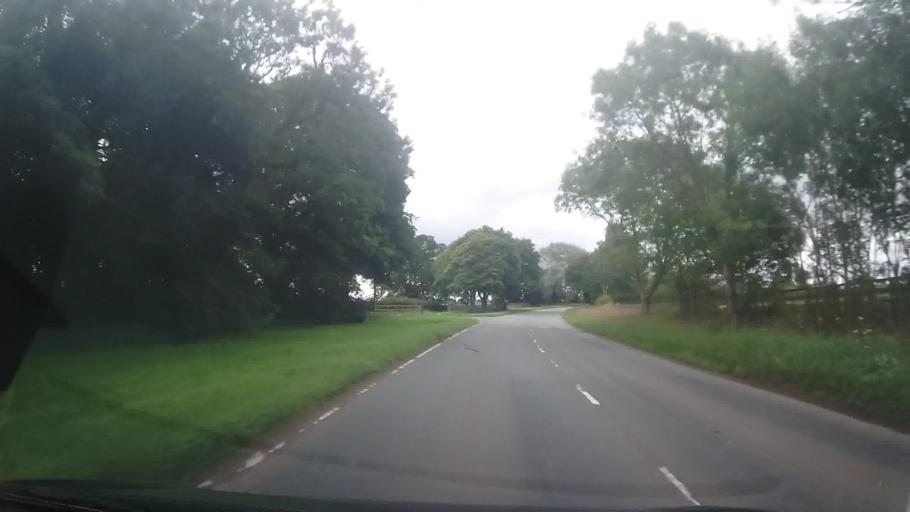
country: GB
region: England
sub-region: Cheshire West and Chester
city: Malpas
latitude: 52.9378
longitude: -2.7907
